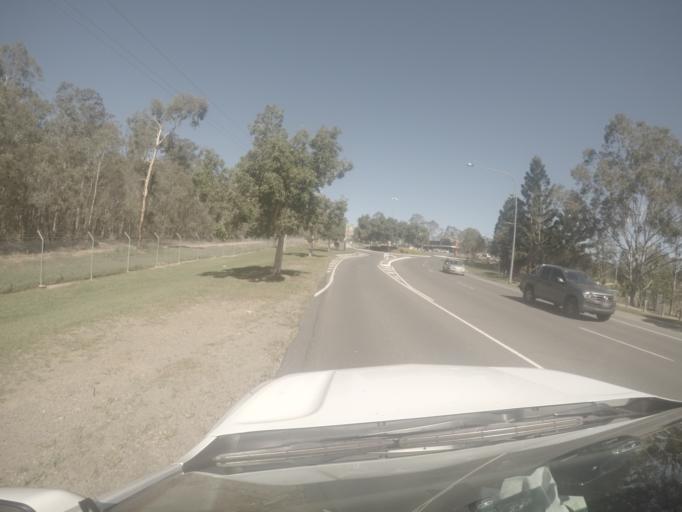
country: AU
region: Queensland
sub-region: Ipswich
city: Springfield
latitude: -27.6501
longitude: 152.9208
